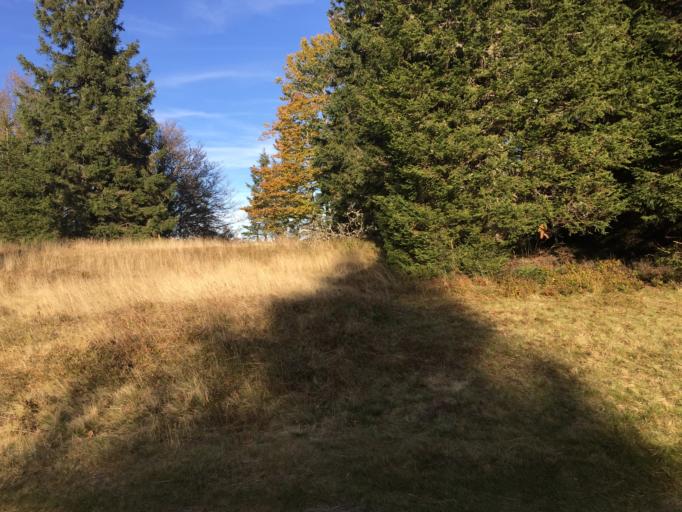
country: SI
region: Mislinja
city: Mislinja
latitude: 46.4983
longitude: 15.2164
